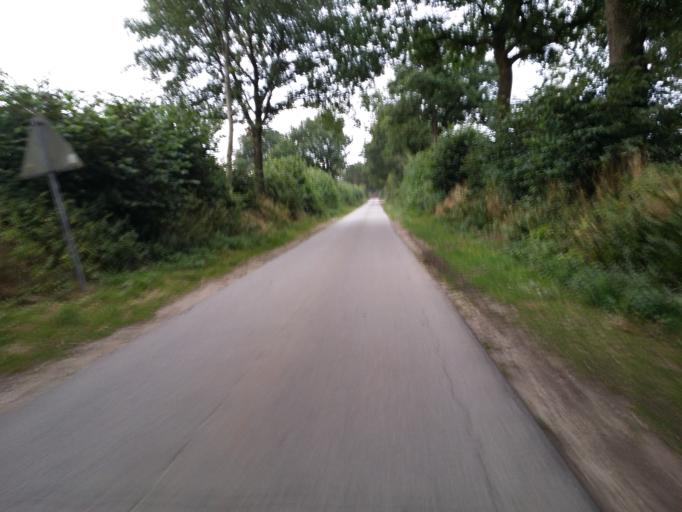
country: DE
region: Schleswig-Holstein
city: Kleve
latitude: 53.9835
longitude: 9.4117
